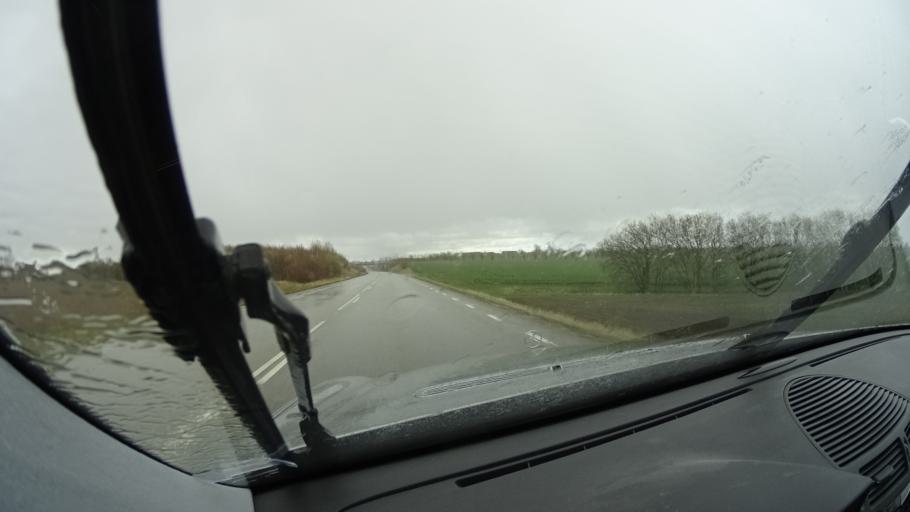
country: SE
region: Skane
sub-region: Lunds Kommun
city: Lund
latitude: 55.7451
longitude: 13.1881
